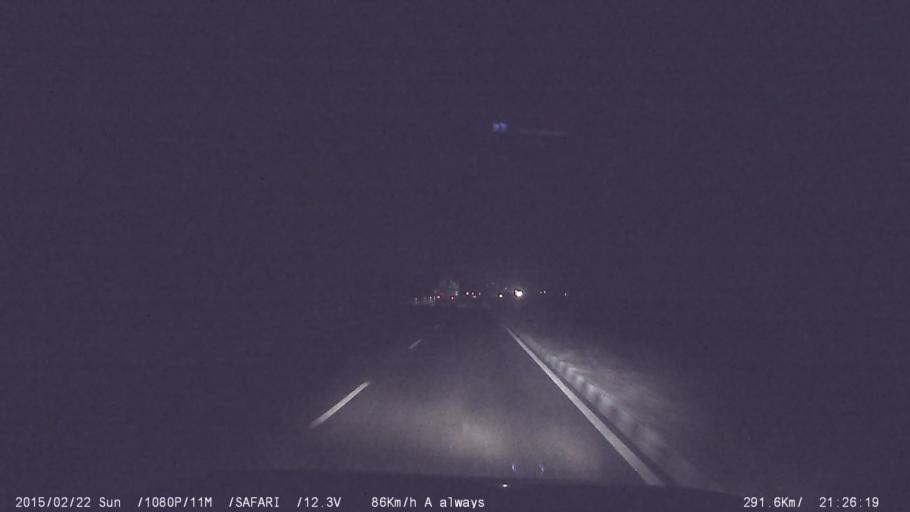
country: IN
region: Tamil Nadu
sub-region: Karur
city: Karur
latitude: 10.9038
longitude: 78.0353
